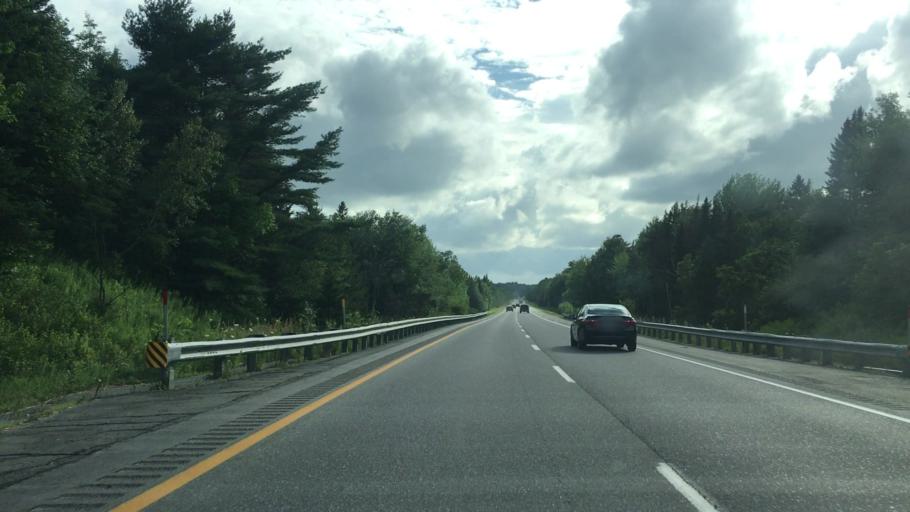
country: US
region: Maine
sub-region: Somerset County
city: Palmyra
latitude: 44.8146
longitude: -69.3433
